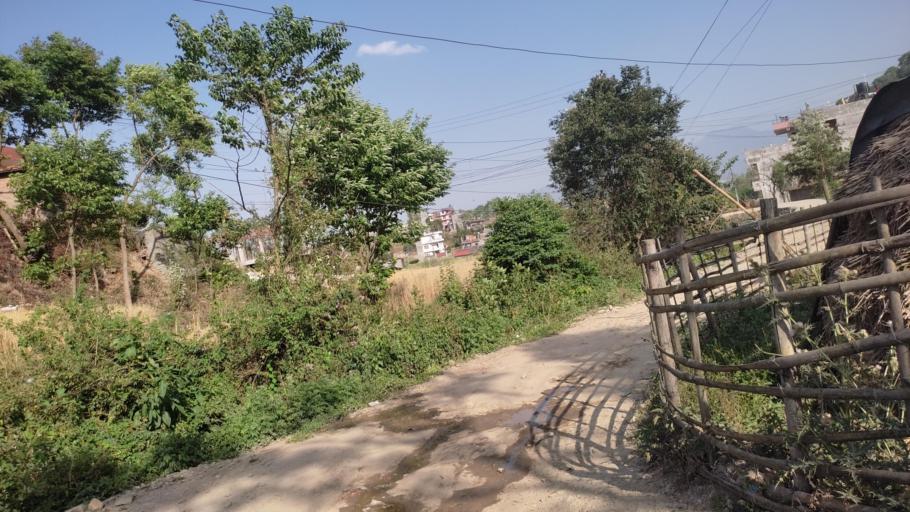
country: NP
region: Central Region
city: Kirtipur
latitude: 27.6598
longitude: 85.2641
